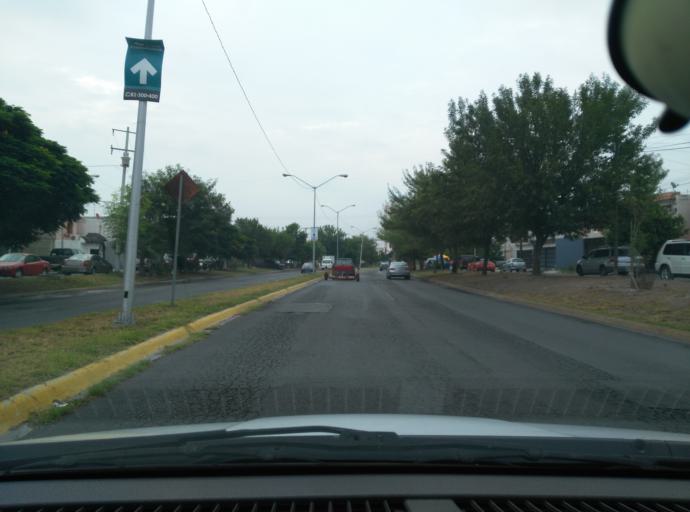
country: MX
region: Nuevo Leon
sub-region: Apodaca
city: Fraccionamiento Cosmopolis Octavo Sector
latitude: 25.7713
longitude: -100.2516
